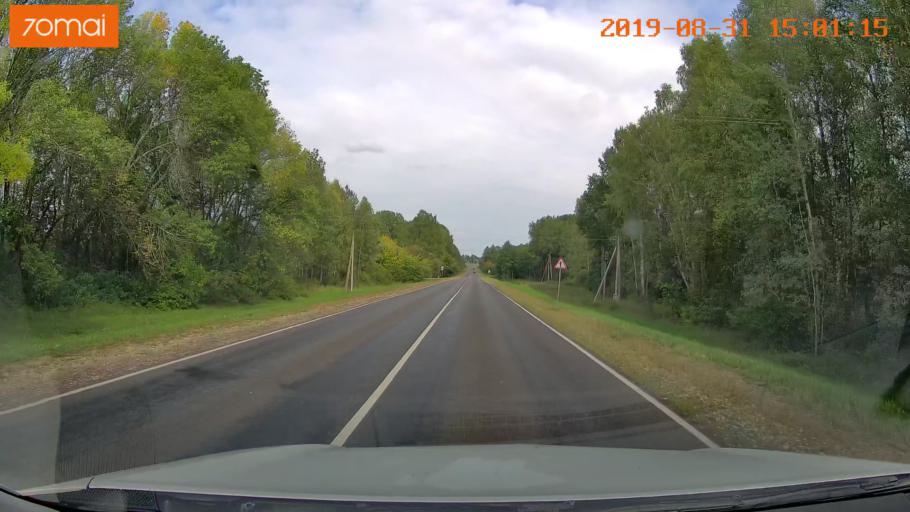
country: RU
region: Kaluga
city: Spas-Demensk
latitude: 54.3380
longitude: 34.0519
